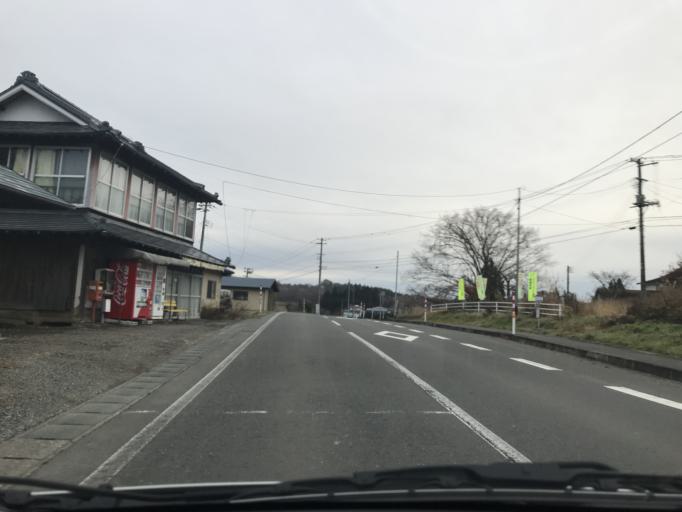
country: JP
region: Iwate
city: Kitakami
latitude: 39.2770
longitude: 141.2661
